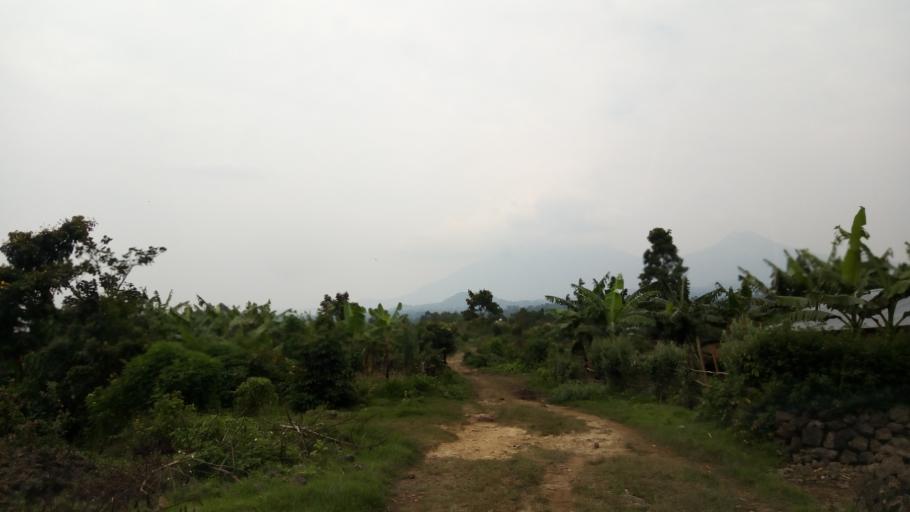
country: UG
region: Western Region
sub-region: Kisoro District
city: Kisoro
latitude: -1.2657
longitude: 29.6109
